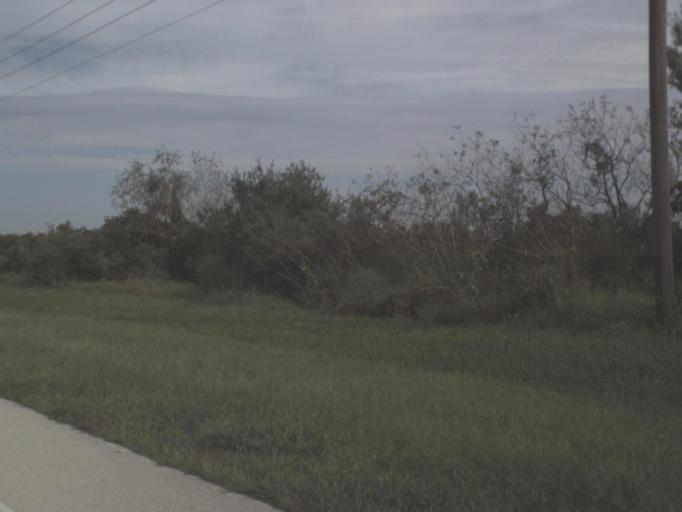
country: US
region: Florida
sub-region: DeSoto County
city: Southeast Arcadia
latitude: 27.1576
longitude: -81.8139
